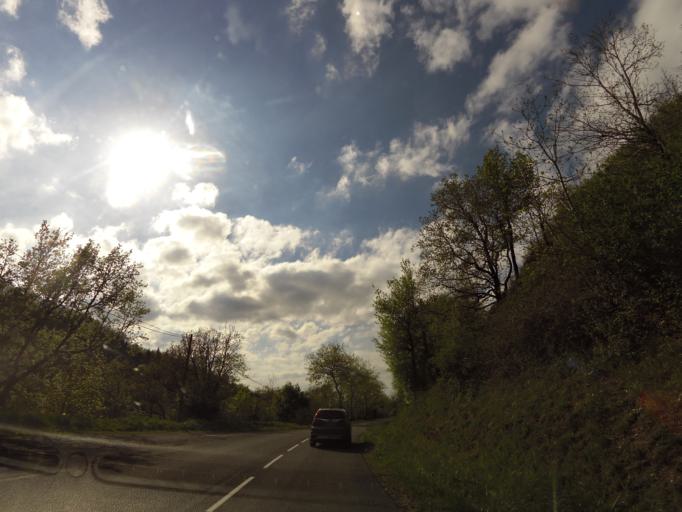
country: FR
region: Midi-Pyrenees
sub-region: Departement du Tarn
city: Soreze
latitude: 43.4312
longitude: 2.0529
